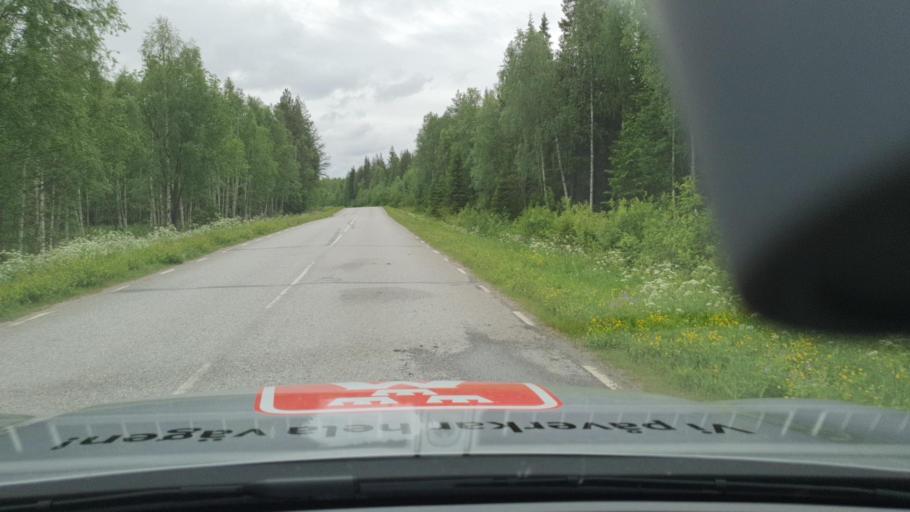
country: SE
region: Norrbotten
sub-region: Lulea Kommun
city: Ranea
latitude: 65.8880
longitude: 22.1937
